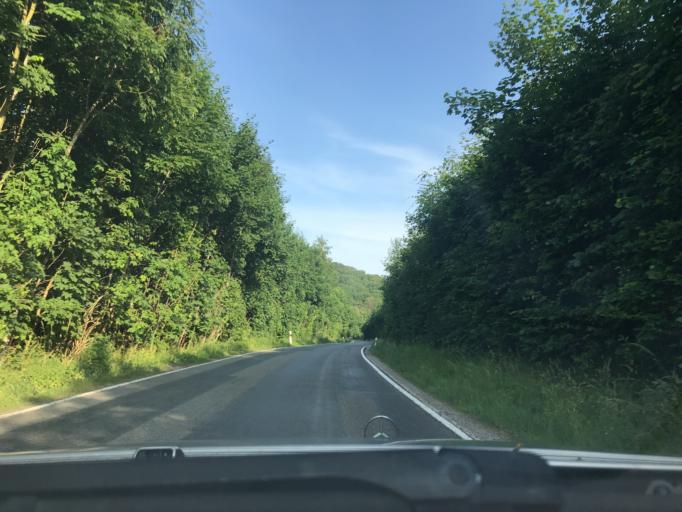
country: DE
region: Thuringia
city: Kleinbartloff
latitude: 51.3436
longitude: 10.3661
